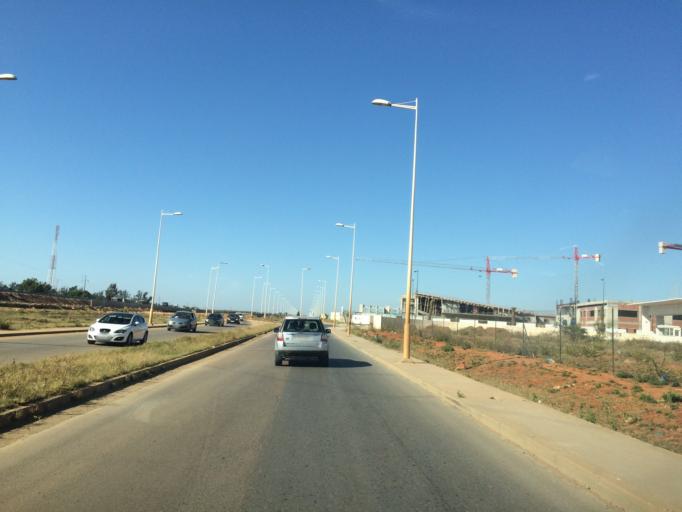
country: MA
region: Rabat-Sale-Zemmour-Zaer
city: Sale
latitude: 33.9870
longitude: -6.7284
